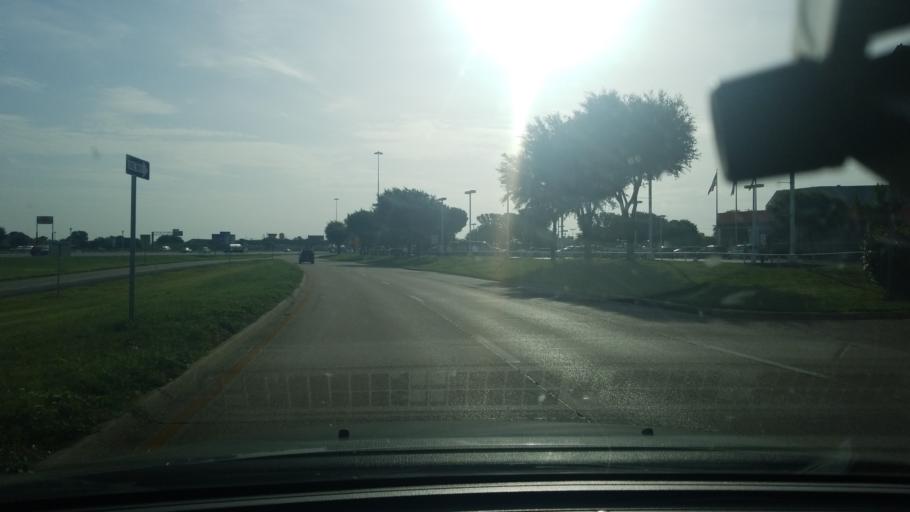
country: US
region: Texas
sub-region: Dallas County
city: Balch Springs
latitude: 32.7938
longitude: -96.6957
